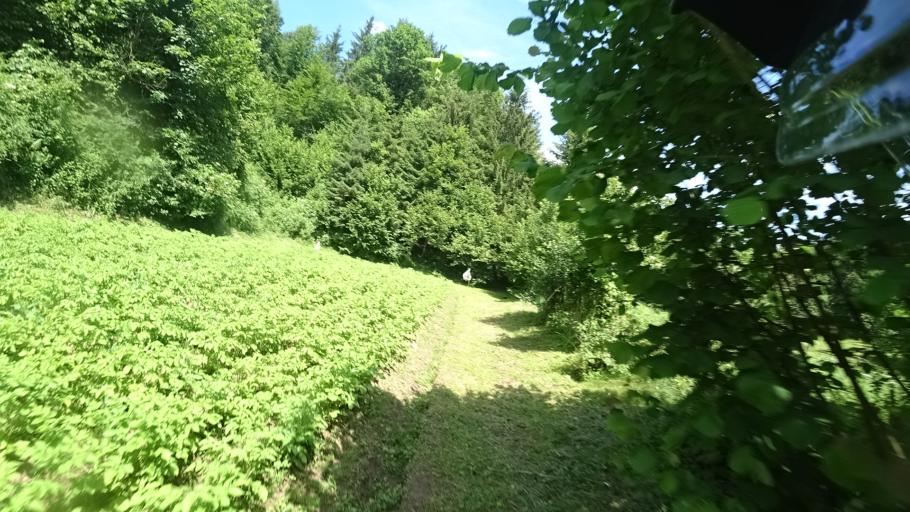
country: SI
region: Osilnica
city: Osilnica
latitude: 45.5142
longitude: 14.6476
